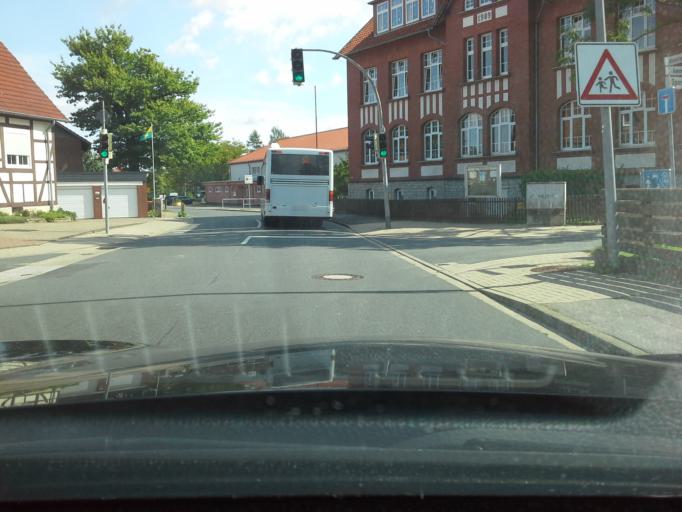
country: DE
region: Lower Saxony
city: Egestorf
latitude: 52.2870
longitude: 9.5083
